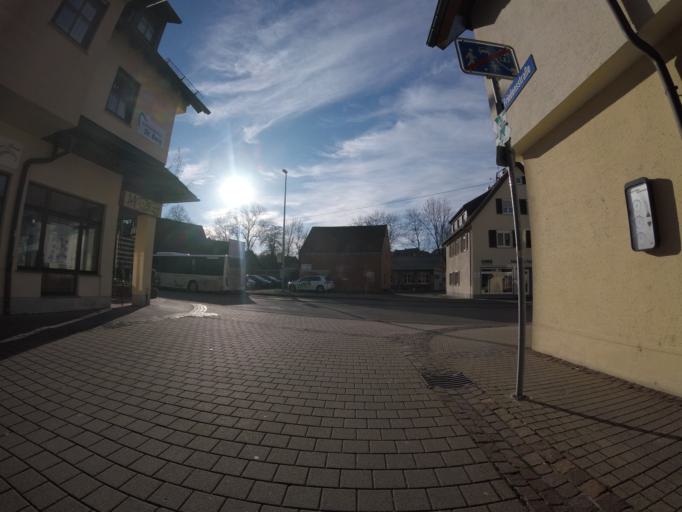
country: DE
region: Baden-Wuerttemberg
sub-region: Regierungsbezirk Stuttgart
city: Allmersbach im Tal
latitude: 48.9294
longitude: 9.4791
